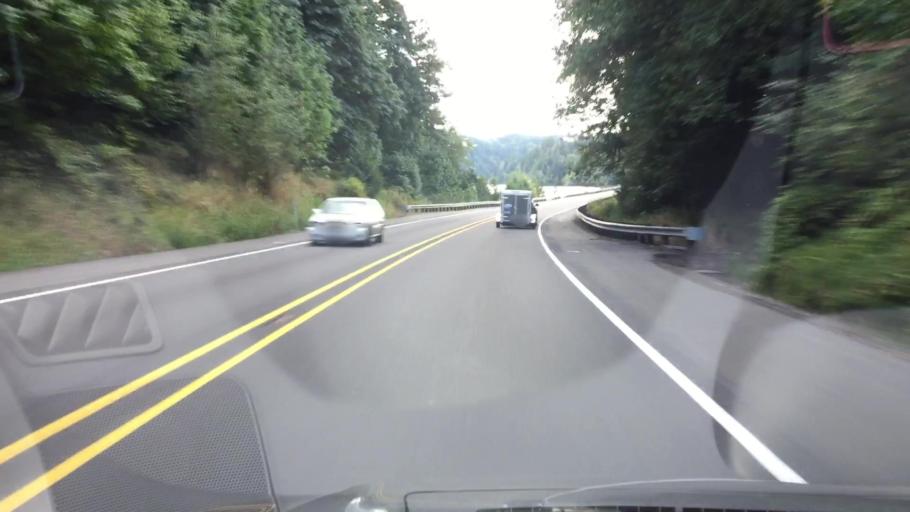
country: US
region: Washington
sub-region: Lewis County
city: Morton
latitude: 46.5175
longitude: -122.5611
